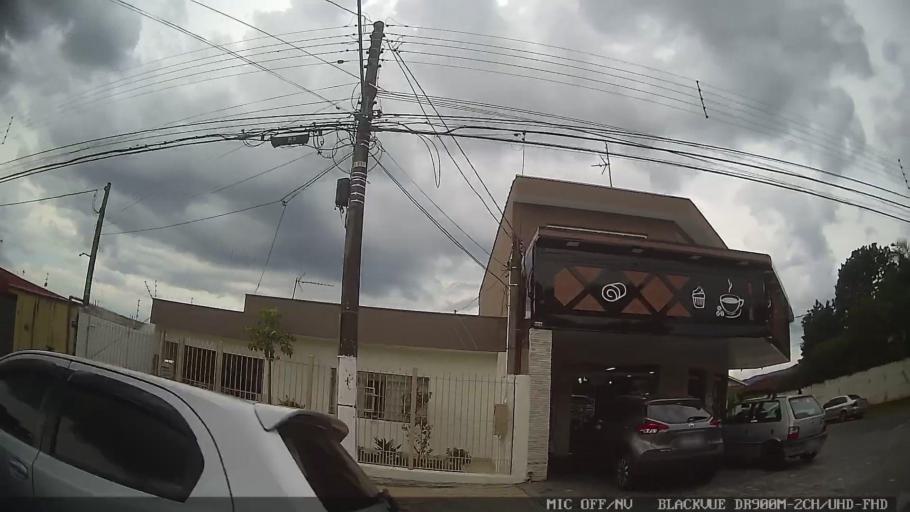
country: BR
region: Sao Paulo
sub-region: Atibaia
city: Atibaia
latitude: -23.1304
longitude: -46.5629
